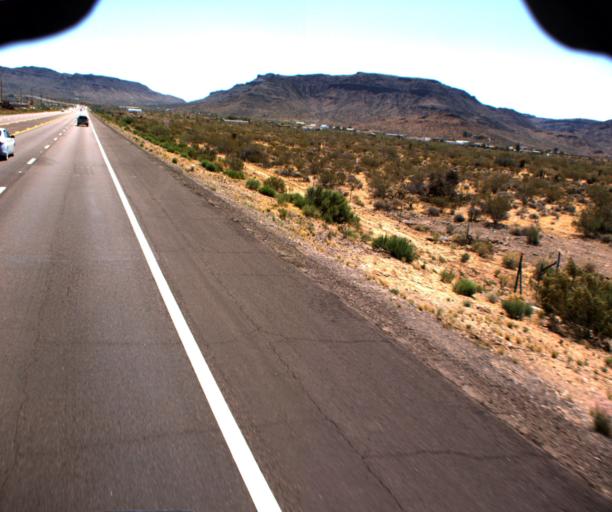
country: US
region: Arizona
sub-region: Mohave County
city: Golden Valley
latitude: 35.2193
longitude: -114.1608
